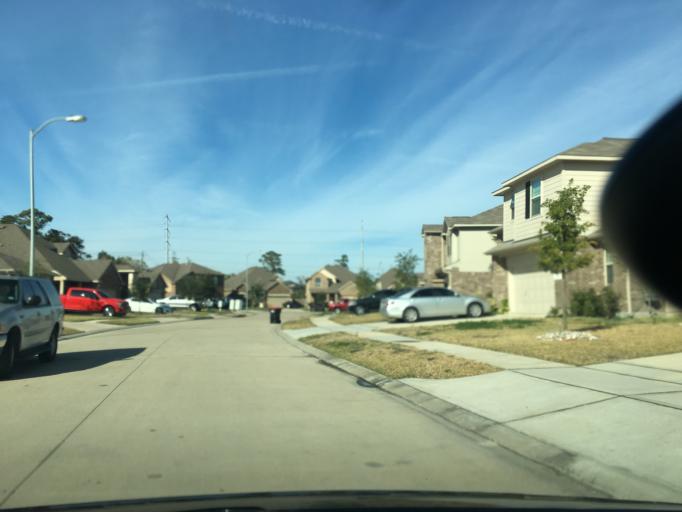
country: US
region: Texas
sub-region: Harris County
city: Cloverleaf
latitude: 29.8147
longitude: -95.1612
